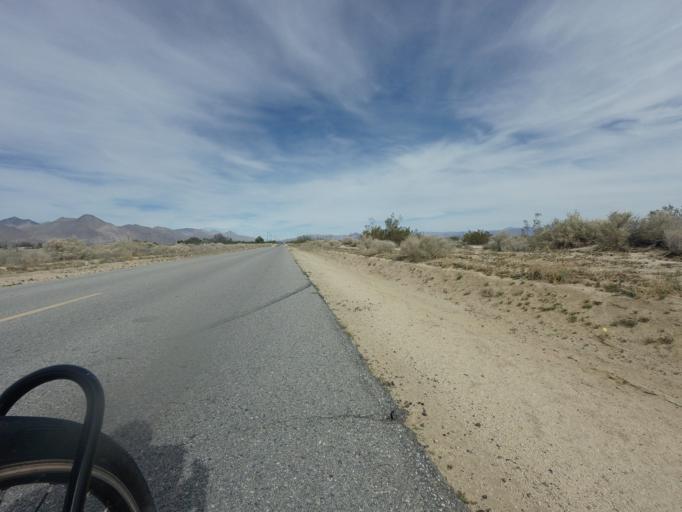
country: US
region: California
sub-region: Kern County
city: Inyokern
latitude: 35.7224
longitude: -117.8347
